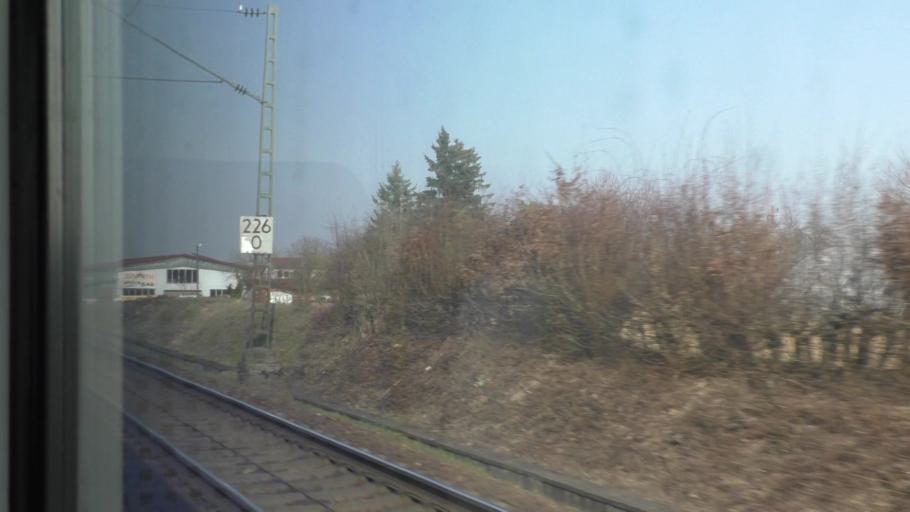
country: DE
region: Baden-Wuerttemberg
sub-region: Freiburg Region
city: Eschbach
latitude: 47.8993
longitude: 7.6688
